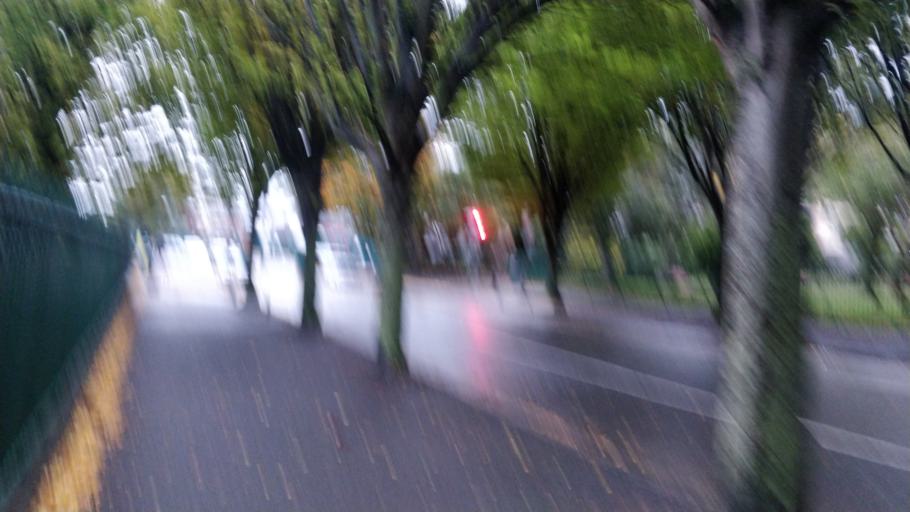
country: IE
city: Clonskeagh
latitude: 53.3276
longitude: -6.2331
